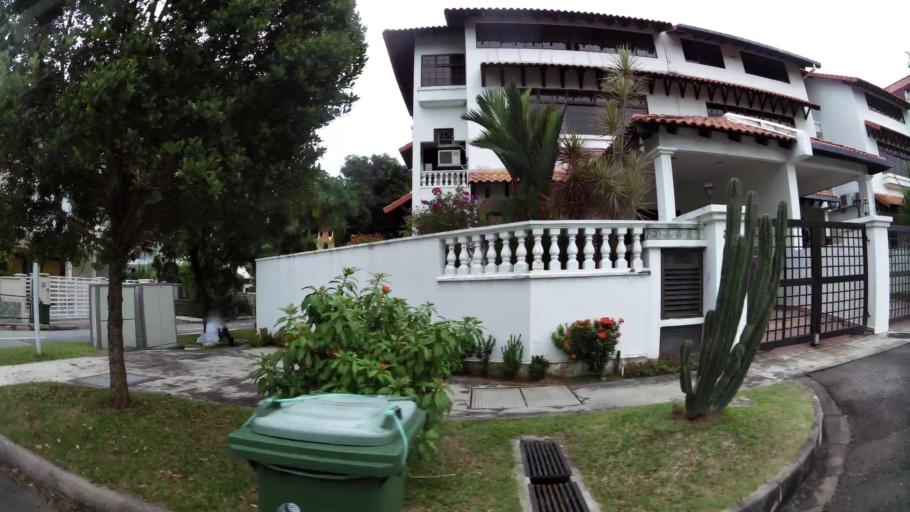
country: SG
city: Singapore
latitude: 1.3634
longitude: 103.8783
